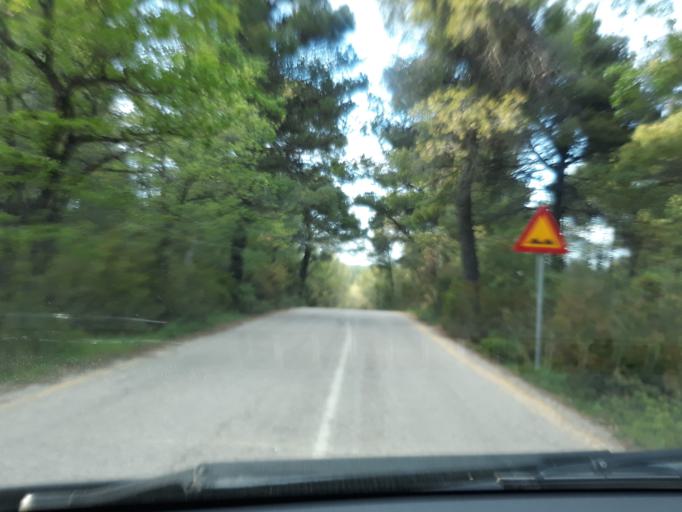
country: GR
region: Attica
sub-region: Nomarchia Anatolikis Attikis
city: Afidnes
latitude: 38.1945
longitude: 23.7837
